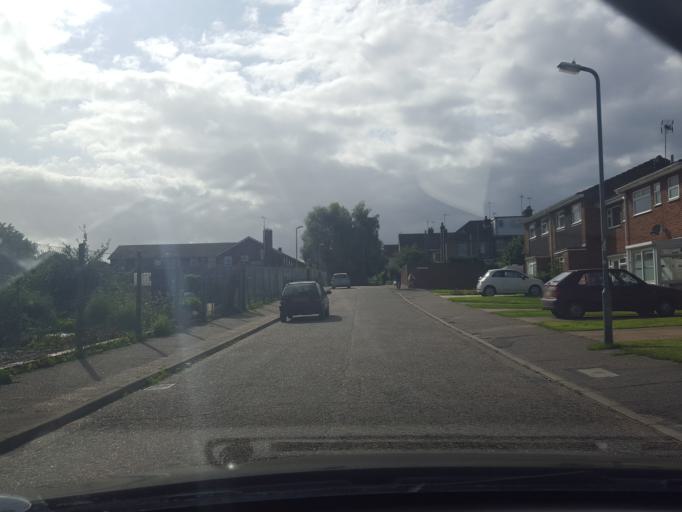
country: GB
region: England
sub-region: Essex
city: Dovercourt
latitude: 51.9337
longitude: 1.2714
